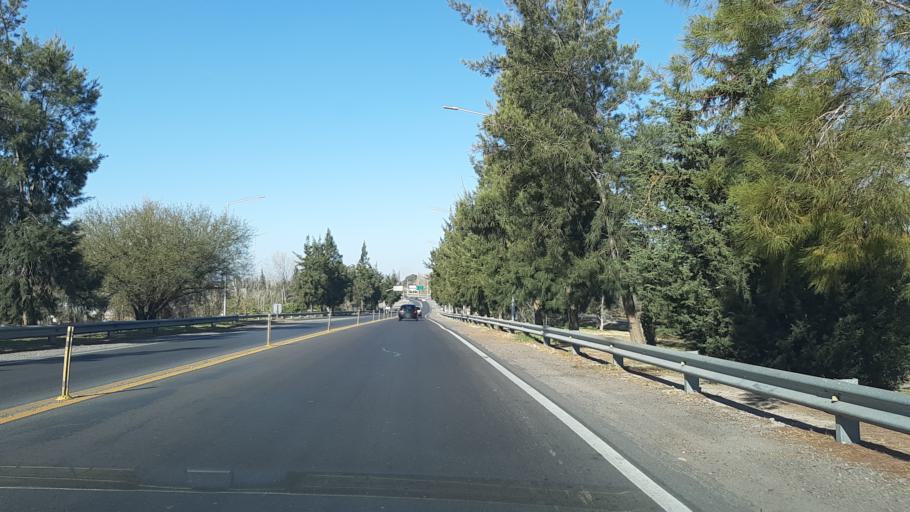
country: AR
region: San Juan
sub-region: Departamento de Santa Lucia
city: Santa Lucia
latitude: -31.5486
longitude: -68.5043
